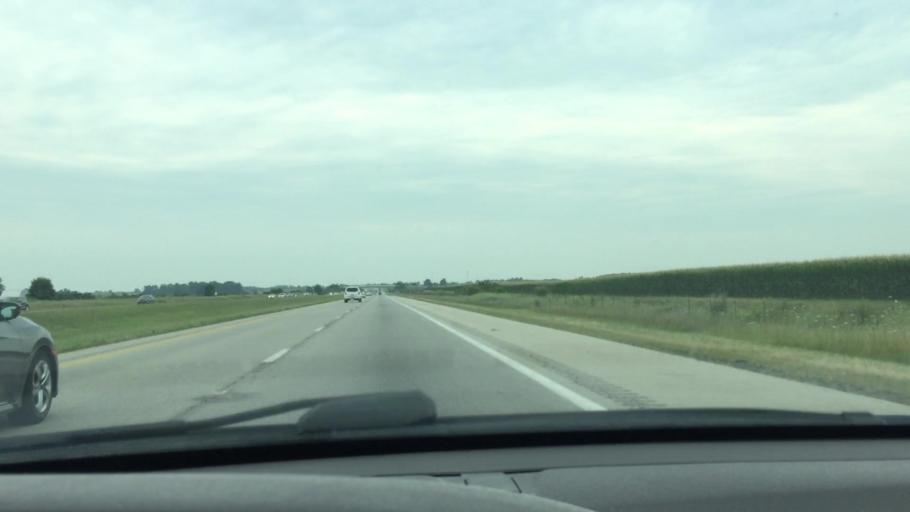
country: US
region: Ohio
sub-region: Greene County
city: Shawnee Hills
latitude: 39.5431
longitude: -83.7611
